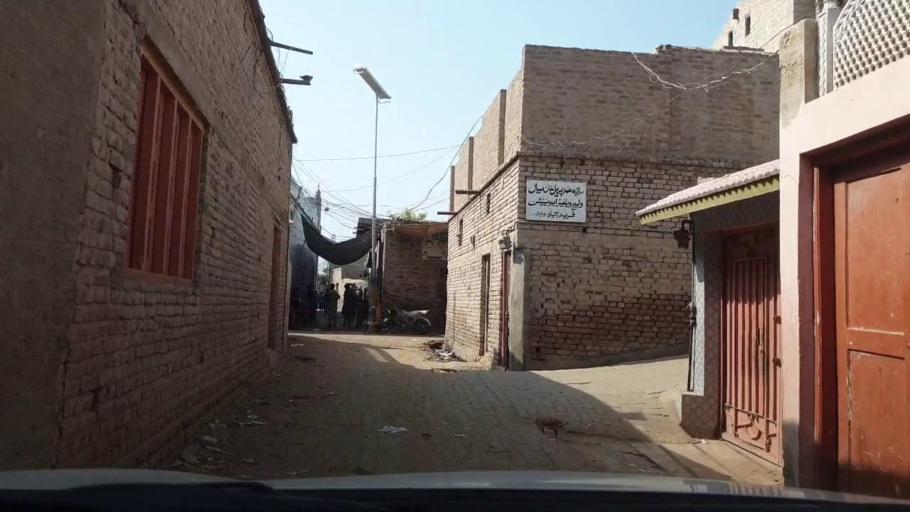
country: PK
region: Sindh
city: Larkana
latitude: 27.4584
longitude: 68.2301
